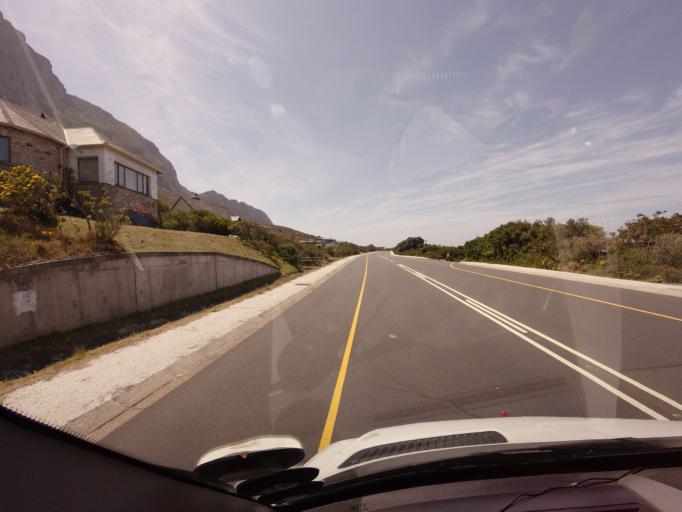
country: ZA
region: Western Cape
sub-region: Overberg District Municipality
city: Grabouw
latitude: -34.3551
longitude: 18.9369
